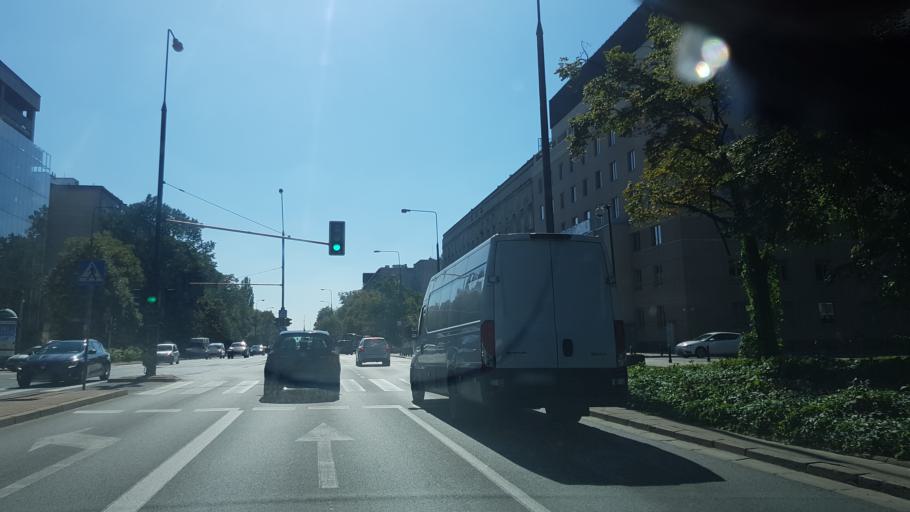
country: PL
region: Masovian Voivodeship
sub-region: Warszawa
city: Warsaw
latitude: 52.2037
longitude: 21.0098
